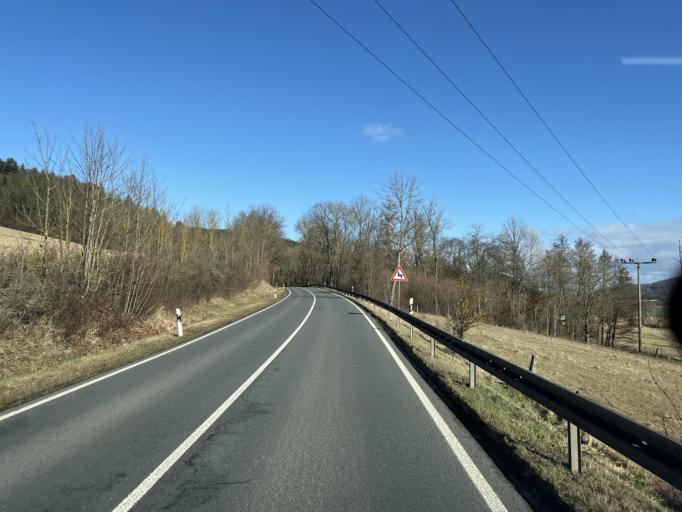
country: DE
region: Thuringia
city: Plaue
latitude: 50.7925
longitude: 10.9104
